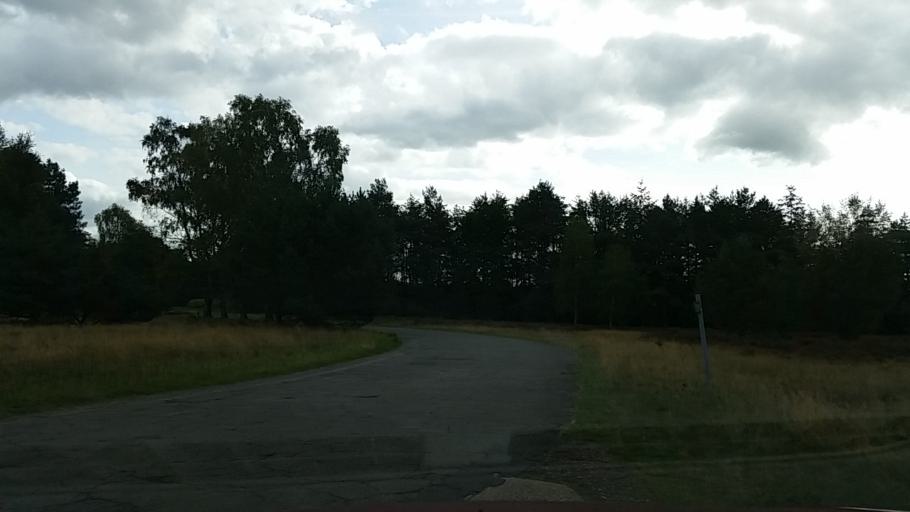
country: DE
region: Lower Saxony
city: Schneverdingen
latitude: 53.1498
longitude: 9.8123
